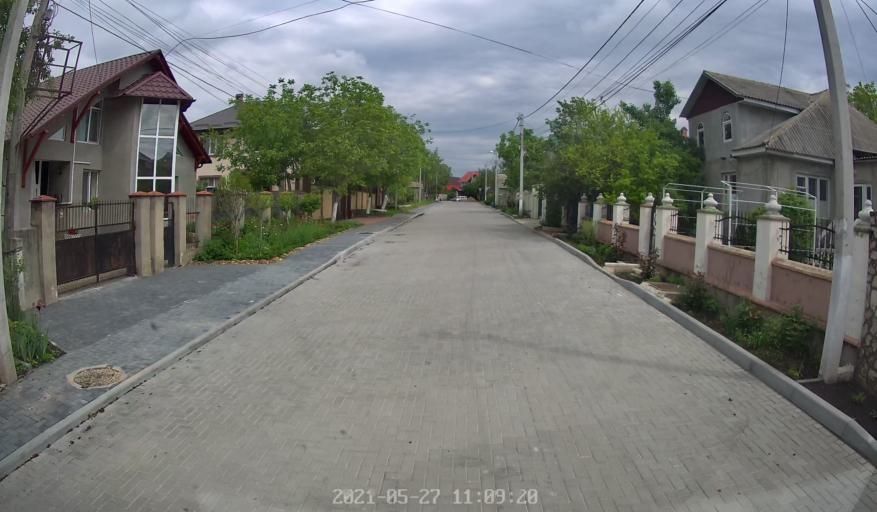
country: MD
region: Chisinau
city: Stauceni
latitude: 47.1009
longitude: 28.8674
